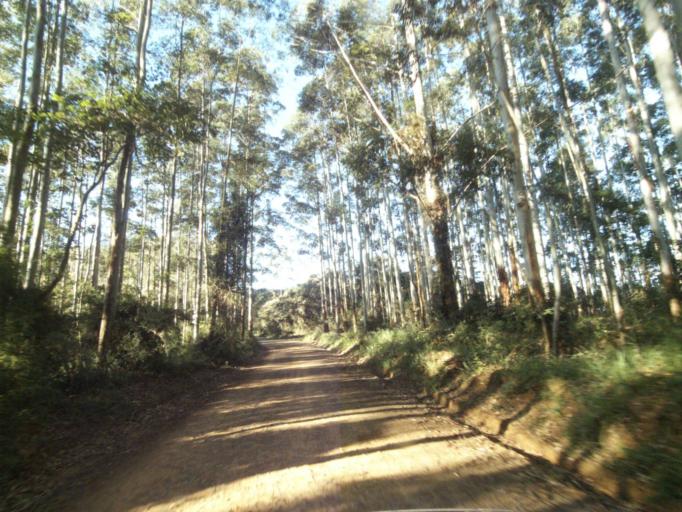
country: BR
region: Parana
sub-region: Telemaco Borba
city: Telemaco Borba
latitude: -24.5061
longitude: -50.5997
